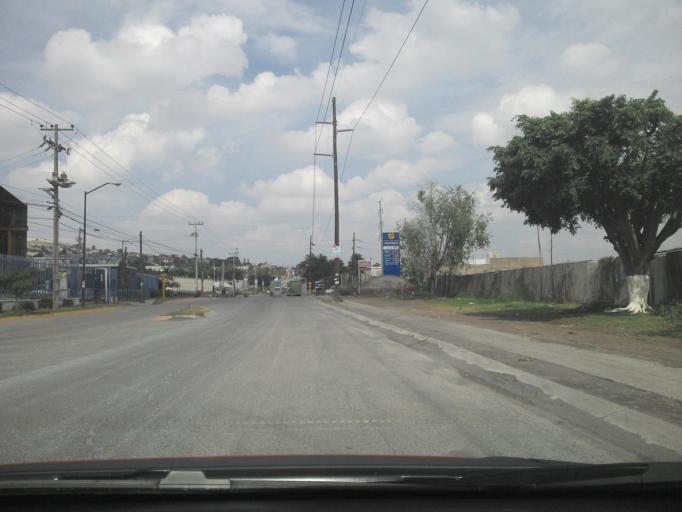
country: MX
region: Jalisco
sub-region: Tlajomulco de Zuniga
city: Altus Bosques
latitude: 20.5816
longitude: -103.3552
